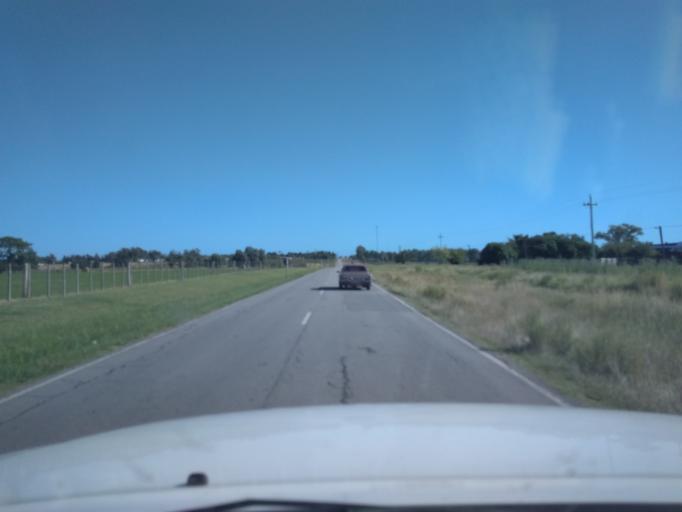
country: UY
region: Canelones
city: San Ramon
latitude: -34.3168
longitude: -55.9593
